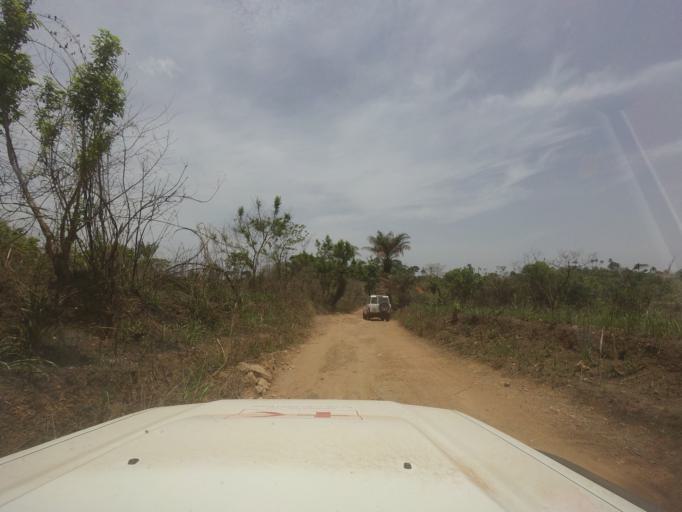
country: SL
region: Eastern Province
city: Buedu
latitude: 8.4888
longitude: -10.3331
